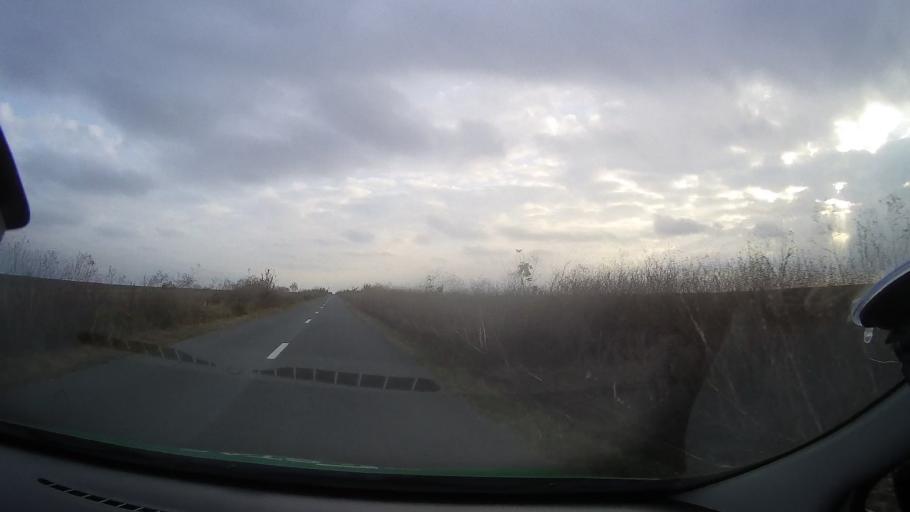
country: RO
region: Constanta
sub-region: Comuna Pestera
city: Pestera
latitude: 44.1446
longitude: 28.1158
